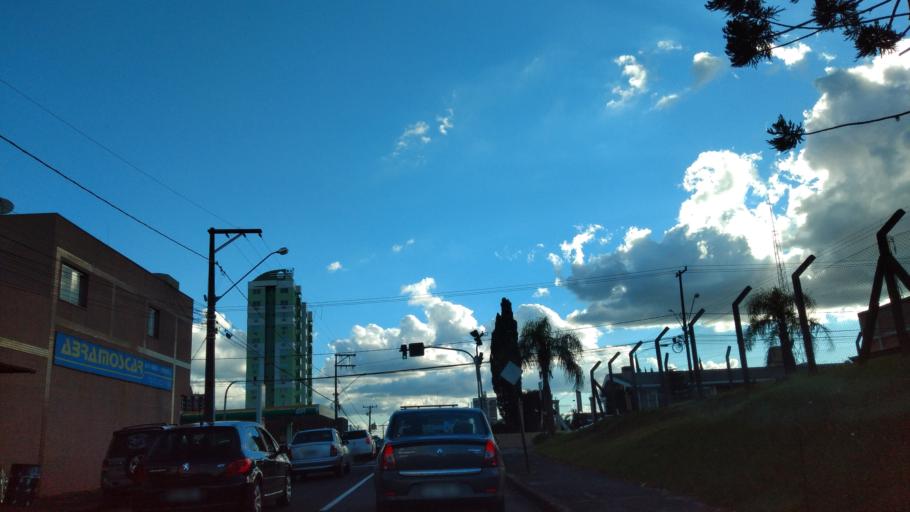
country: BR
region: Parana
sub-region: Guarapuava
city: Guarapuava
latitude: -25.3871
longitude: -51.4626
